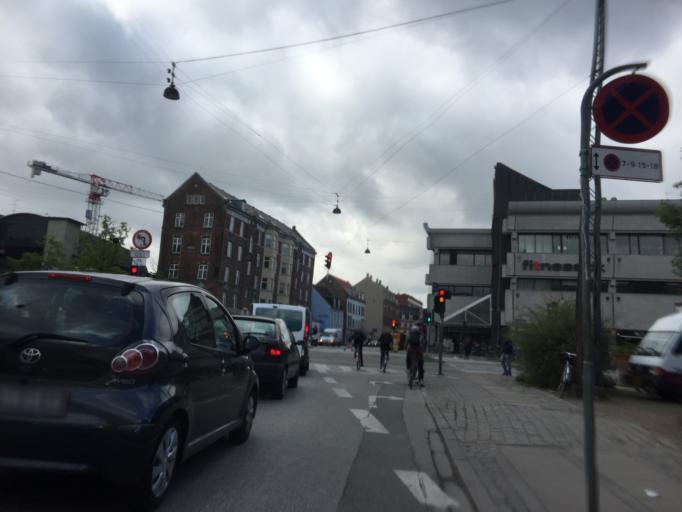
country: DK
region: Capital Region
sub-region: Frederiksberg Kommune
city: Frederiksberg
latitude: 55.7015
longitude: 12.5372
